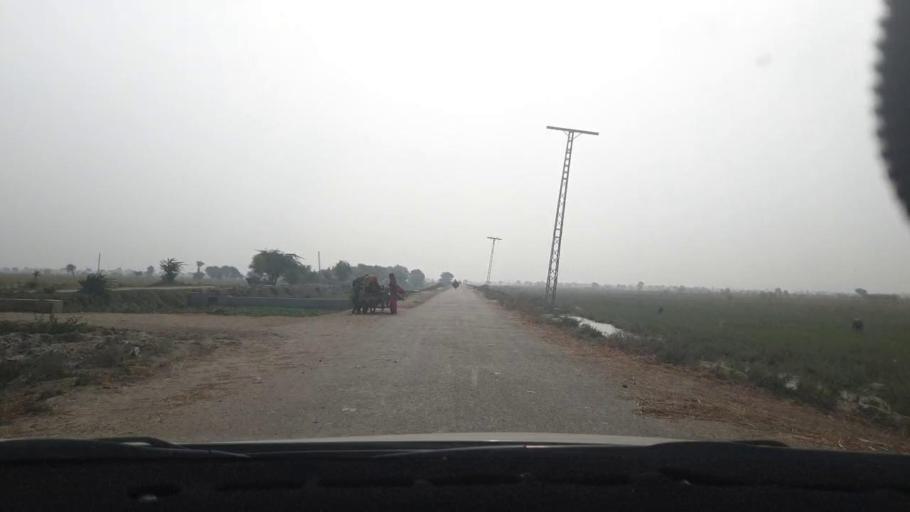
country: PK
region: Sindh
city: Tando Muhammad Khan
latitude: 25.0782
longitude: 68.5326
